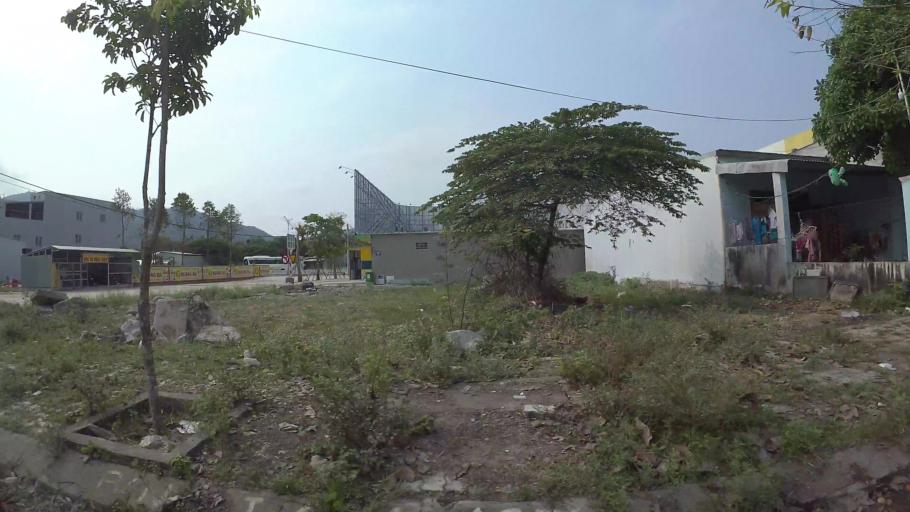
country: VN
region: Da Nang
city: Lien Chieu
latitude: 16.0499
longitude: 108.1500
